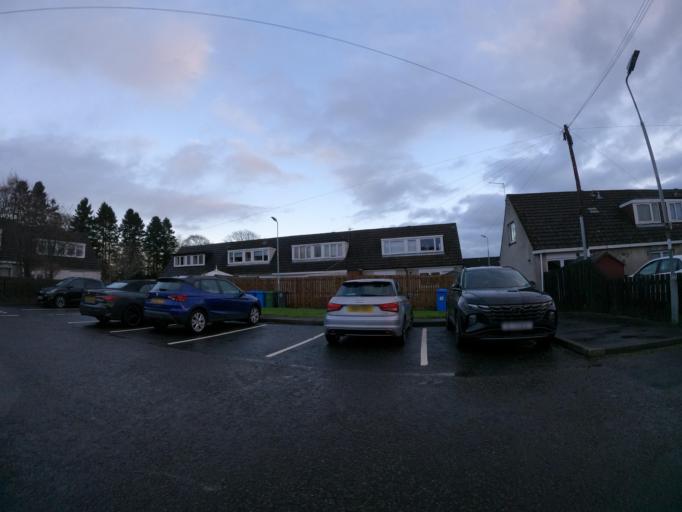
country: GB
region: Scotland
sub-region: West Lothian
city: Livingston
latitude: 55.9270
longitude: -3.5061
